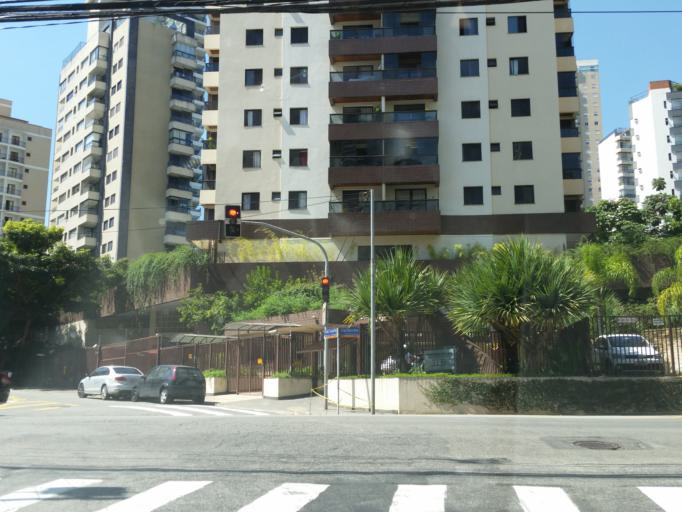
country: BR
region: Sao Paulo
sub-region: Taboao Da Serra
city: Taboao da Serra
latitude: -23.6271
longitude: -46.7366
